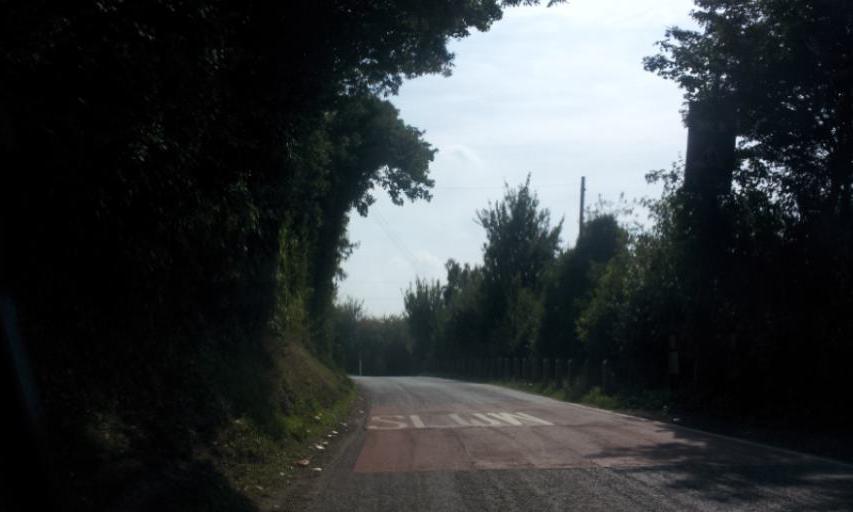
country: GB
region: England
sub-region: Kent
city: Newington
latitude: 51.3391
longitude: 0.6945
